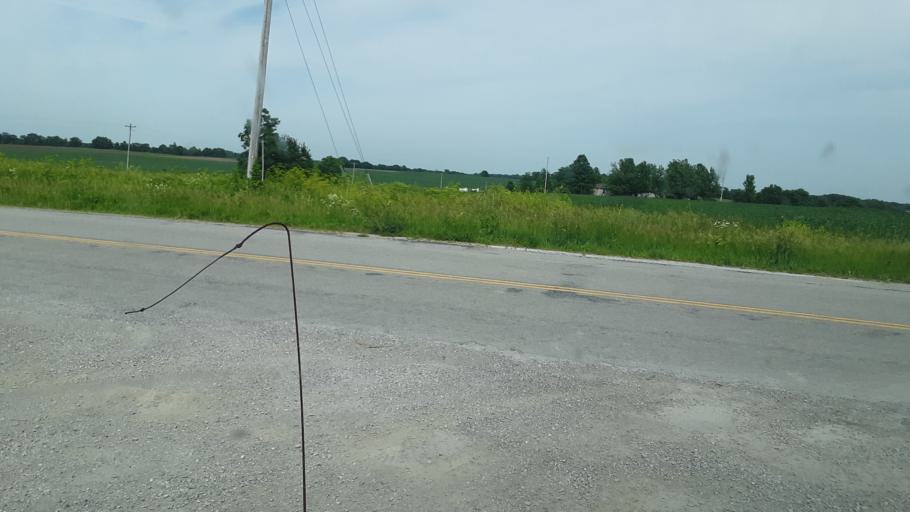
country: US
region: Missouri
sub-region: Saline County
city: Marshall
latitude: 38.9556
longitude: -93.0870
